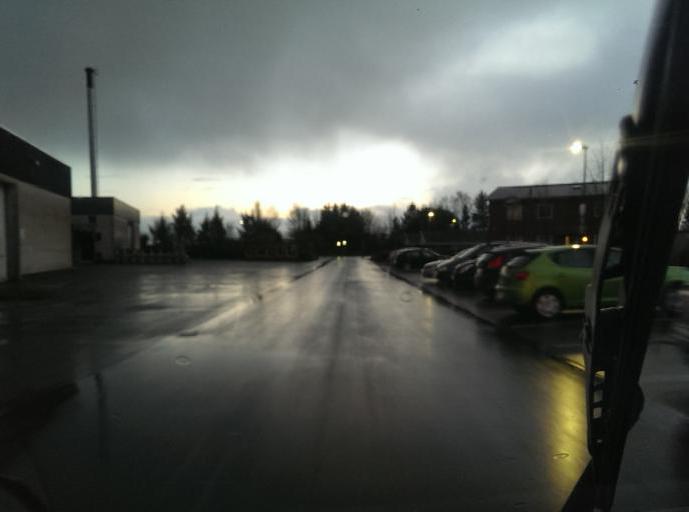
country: DK
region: South Denmark
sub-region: Esbjerg Kommune
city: Bramming
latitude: 55.4652
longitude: 8.6888
